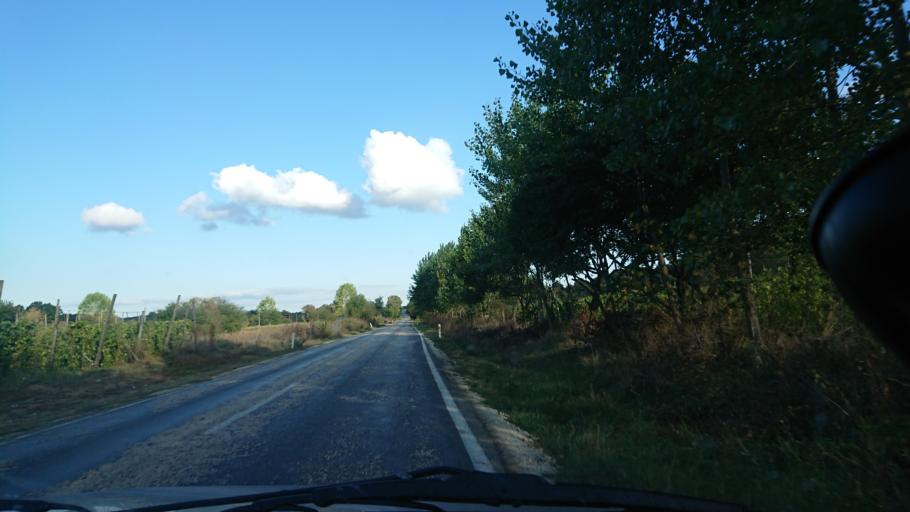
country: TR
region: Bilecik
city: Pazaryeri
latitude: 40.0152
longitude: 29.8423
